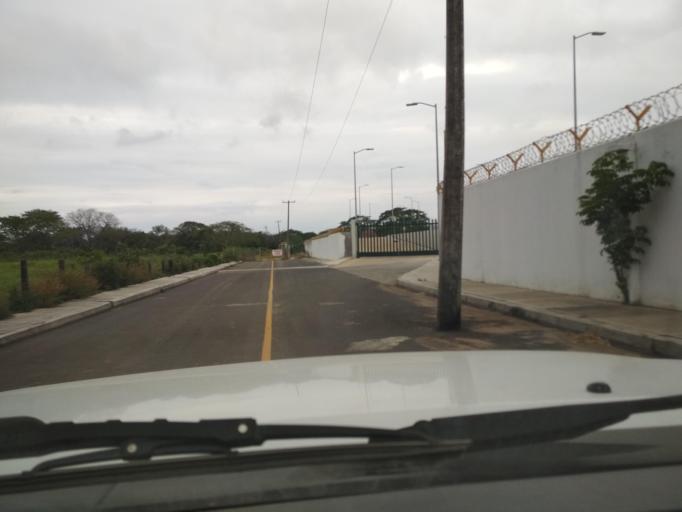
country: MX
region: Veracruz
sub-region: Medellin
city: Fraccionamiento Arboledas San Ramon
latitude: 19.0807
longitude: -96.1405
